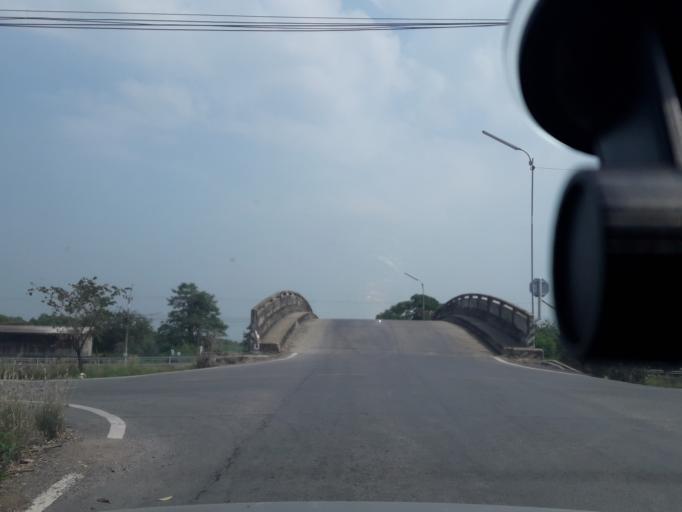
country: TH
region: Pathum Thani
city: Nong Suea
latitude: 14.1966
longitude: 100.8913
